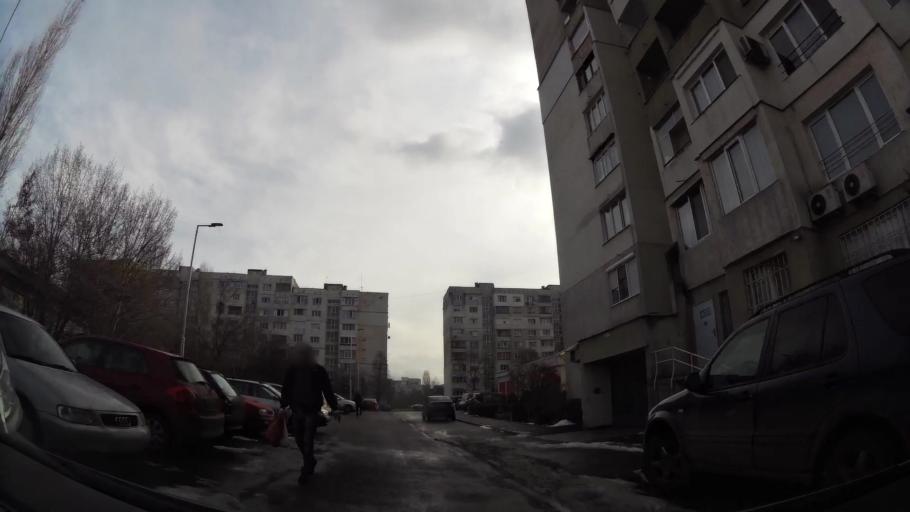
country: BG
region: Sofia-Capital
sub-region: Stolichna Obshtina
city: Sofia
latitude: 42.7180
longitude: 23.2708
